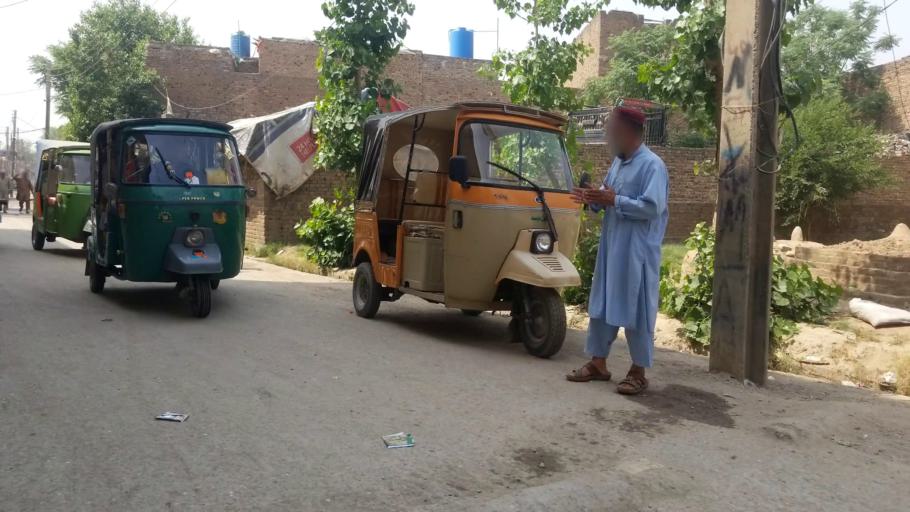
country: PK
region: Khyber Pakhtunkhwa
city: Peshawar
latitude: 33.9854
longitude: 71.5401
